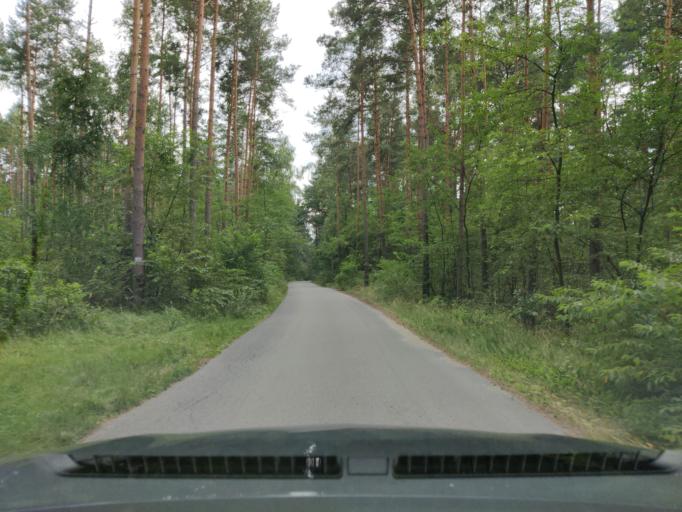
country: PL
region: Masovian Voivodeship
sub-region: Powiat pultuski
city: Pultusk
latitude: 52.7426
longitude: 21.1413
